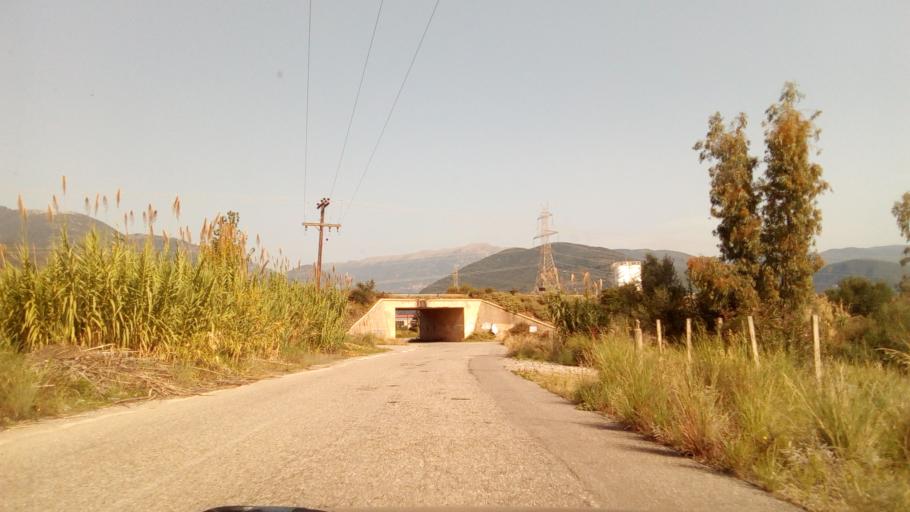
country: GR
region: West Greece
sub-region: Nomos Aitolias kai Akarnanias
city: Nafpaktos
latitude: 38.4071
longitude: 21.8801
